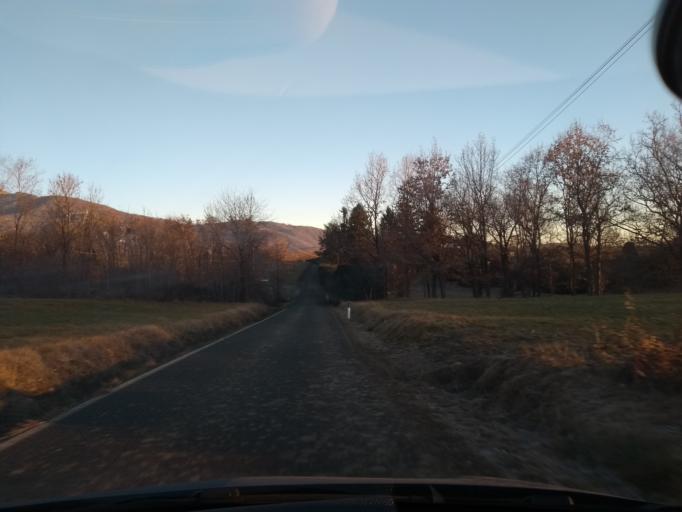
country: IT
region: Piedmont
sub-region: Provincia di Torino
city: Mathi
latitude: 45.2810
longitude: 7.5436
